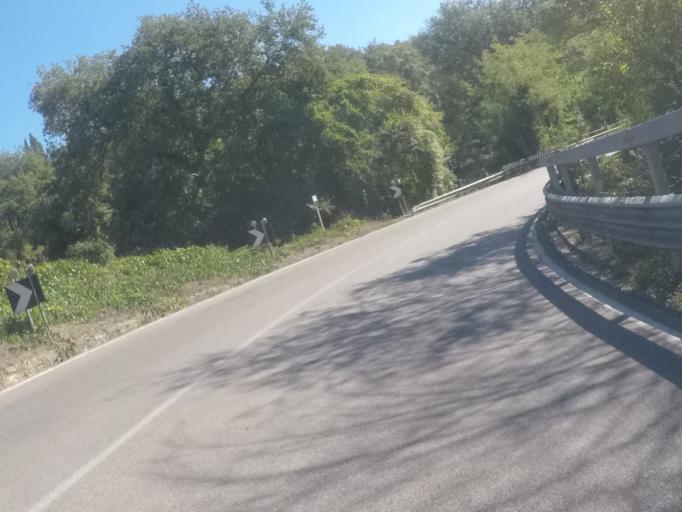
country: IT
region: Tuscany
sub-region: Province of Florence
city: Incisa in Val d'Arno
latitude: 43.6782
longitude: 11.4635
